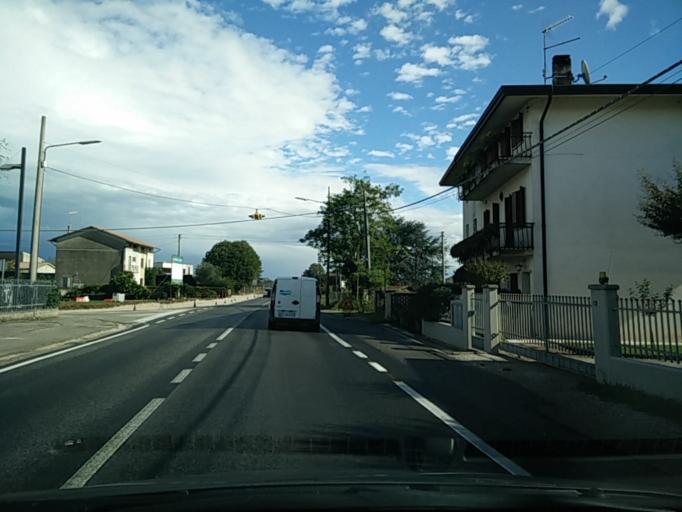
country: IT
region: Veneto
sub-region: Provincia di Treviso
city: Mosnigo
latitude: 45.8625
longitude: 12.0821
